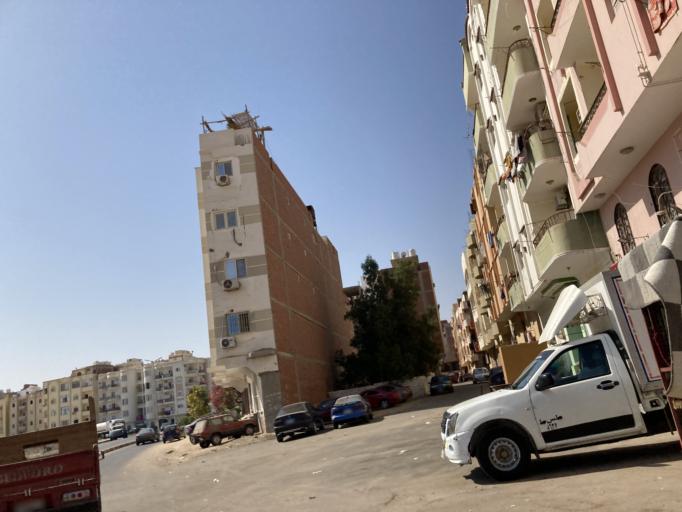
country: EG
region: Red Sea
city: Hurghada
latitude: 27.2487
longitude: 33.8334
